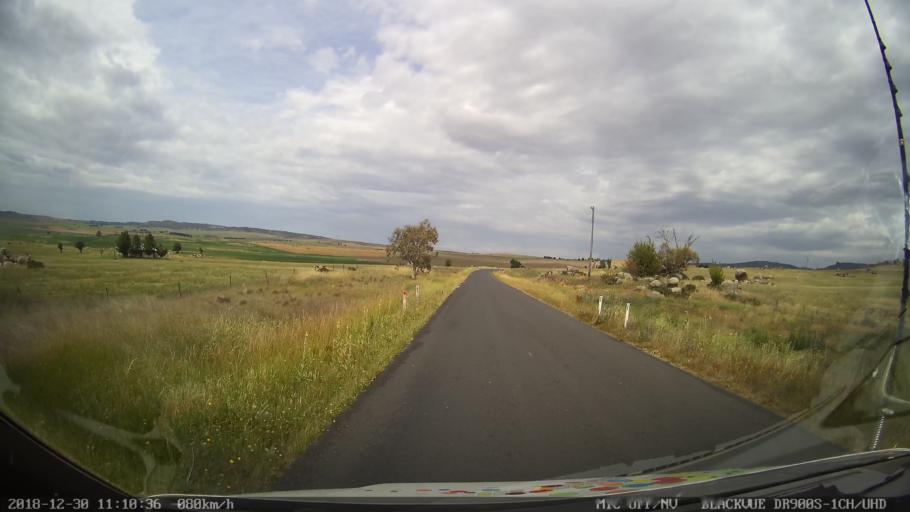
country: AU
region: New South Wales
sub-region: Snowy River
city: Berridale
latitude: -36.5161
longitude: 148.7798
